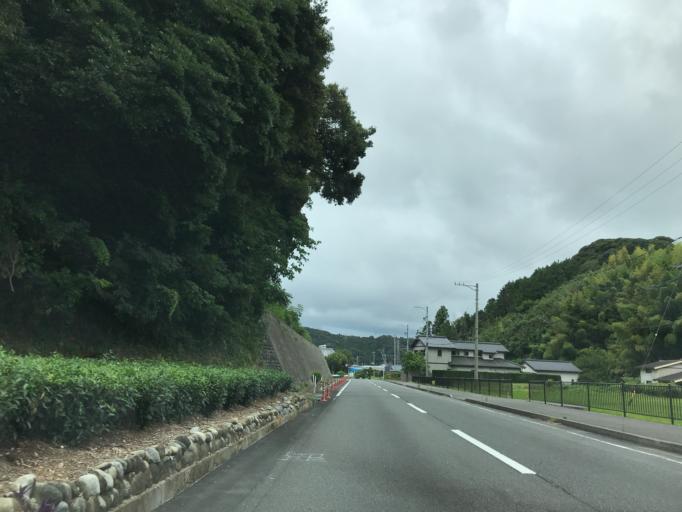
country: JP
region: Shizuoka
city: Sagara
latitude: 34.6675
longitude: 138.1432
